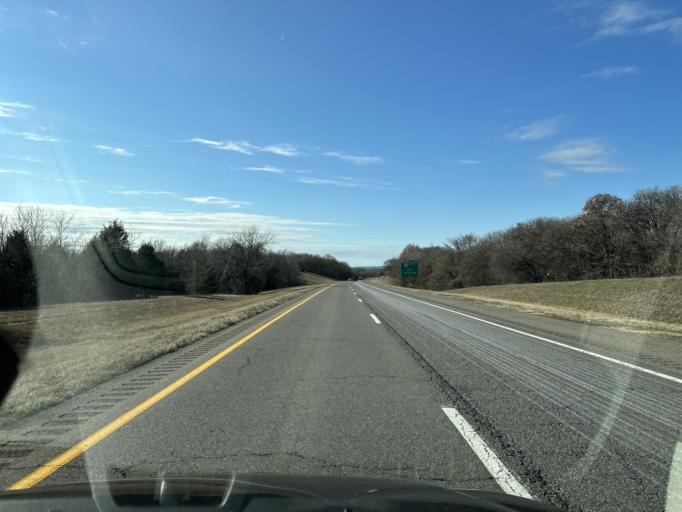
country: US
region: Oklahoma
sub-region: Sequoyah County
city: Vian
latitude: 35.4905
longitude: -95.0687
